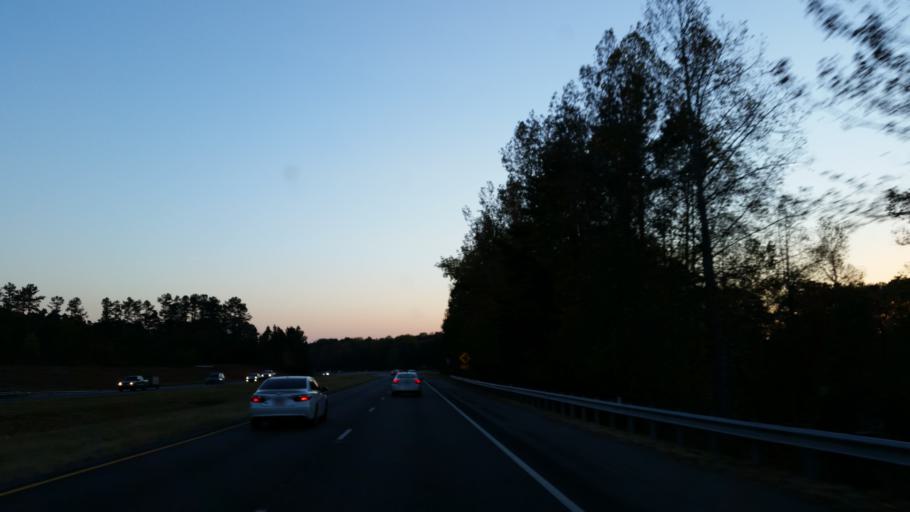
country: US
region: Georgia
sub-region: Forsyth County
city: Cumming
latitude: 34.3061
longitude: -84.0695
